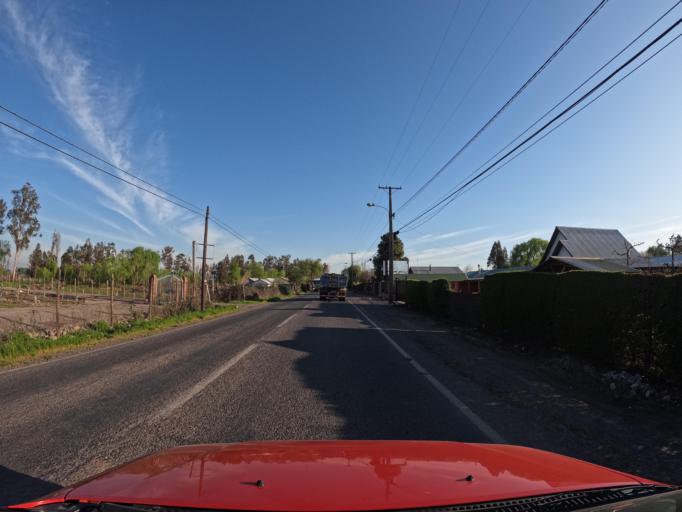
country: CL
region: Maule
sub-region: Provincia de Curico
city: Rauco
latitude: -34.8798
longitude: -71.2695
